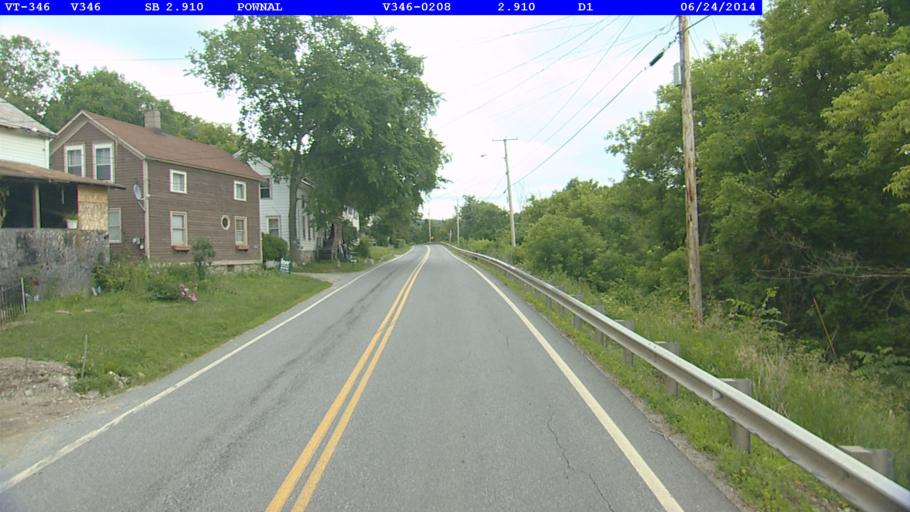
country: US
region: Massachusetts
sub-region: Berkshire County
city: Williamstown
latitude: 42.7965
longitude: -73.2634
